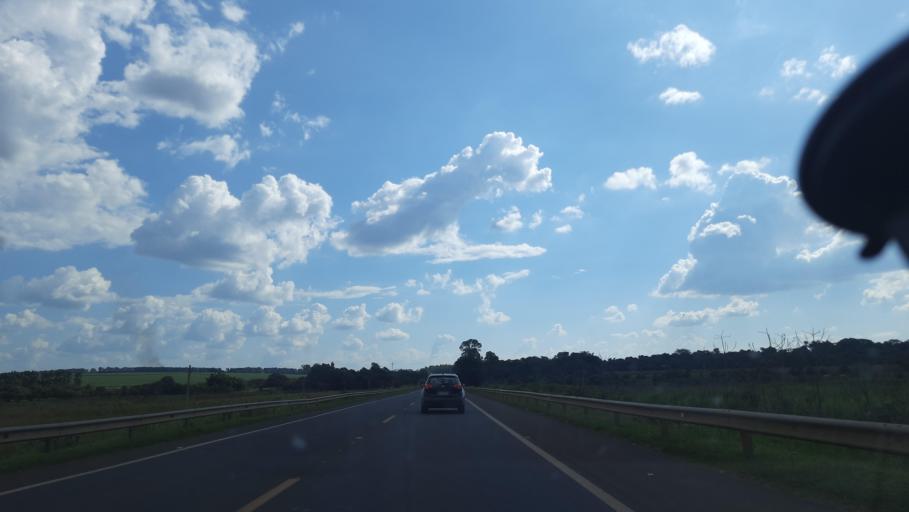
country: BR
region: Sao Paulo
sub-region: Casa Branca
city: Casa Branca
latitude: -21.7478
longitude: -46.9894
